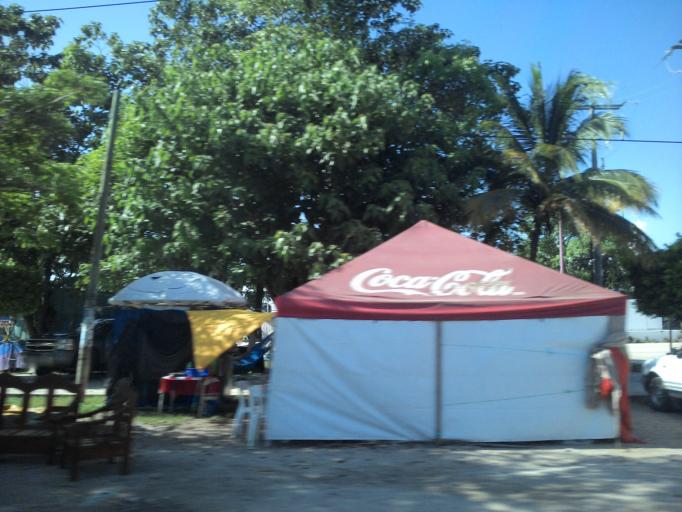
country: MX
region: Chiapas
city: Palenque
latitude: 17.5421
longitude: -91.9899
